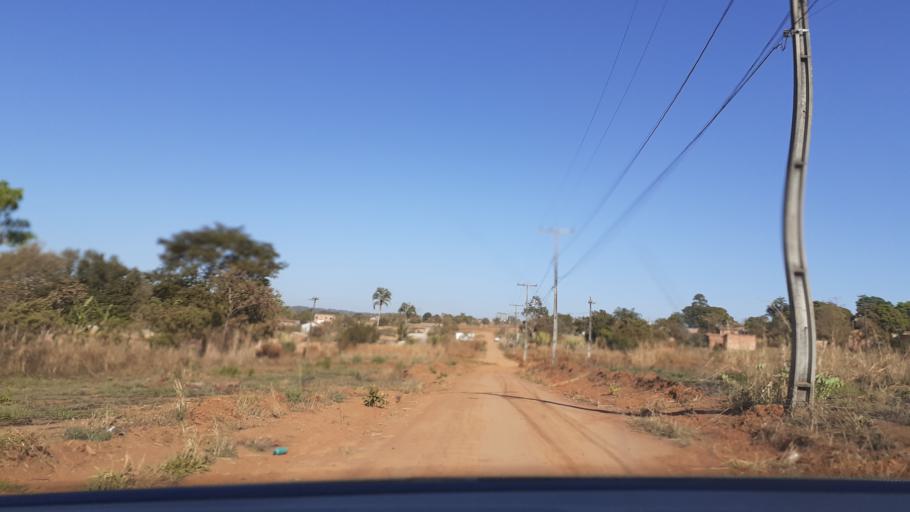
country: BR
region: Goias
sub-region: Aparecida De Goiania
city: Aparecida de Goiania
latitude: -16.8693
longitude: -49.2599
